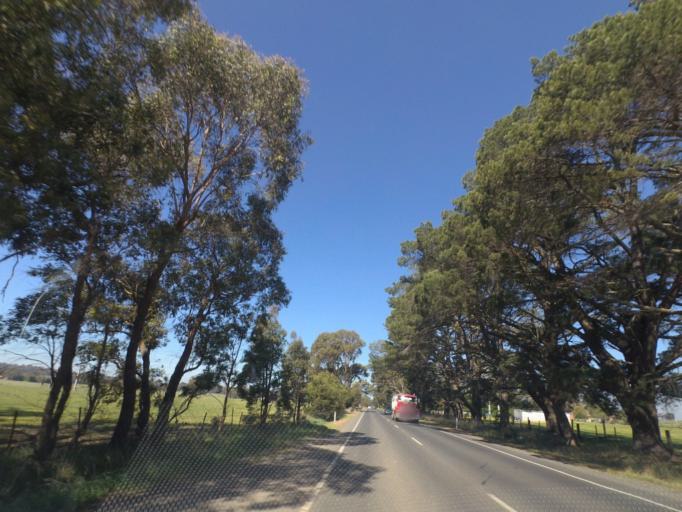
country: AU
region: Victoria
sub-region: Whittlesea
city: Whittlesea
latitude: -37.3265
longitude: 144.9697
